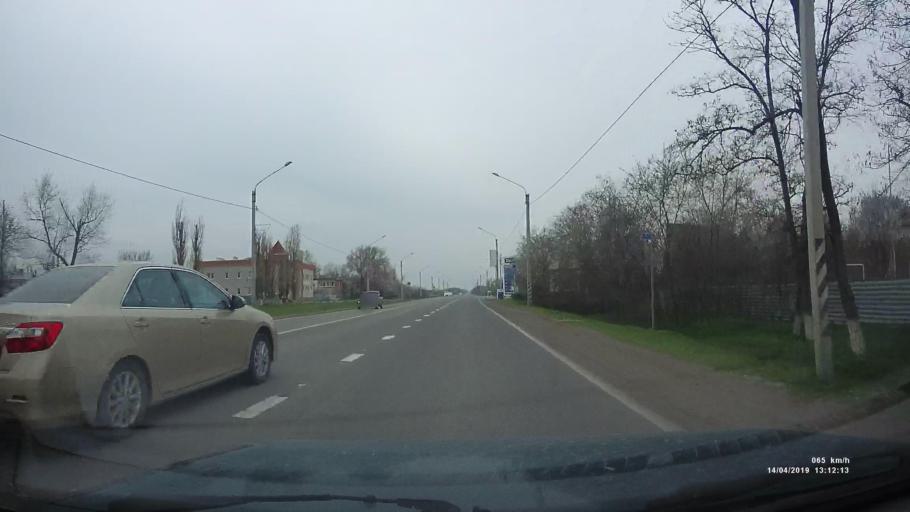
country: RU
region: Rostov
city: Kuleshovka
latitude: 47.1041
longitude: 39.6407
